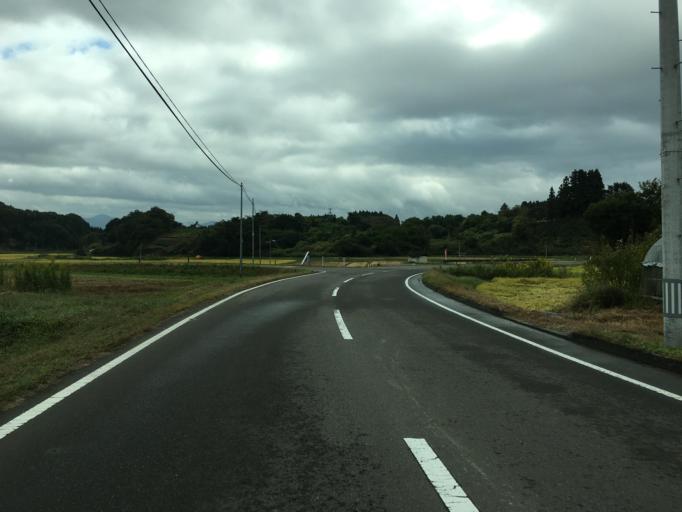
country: JP
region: Fukushima
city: Nihommatsu
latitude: 37.6281
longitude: 140.4444
